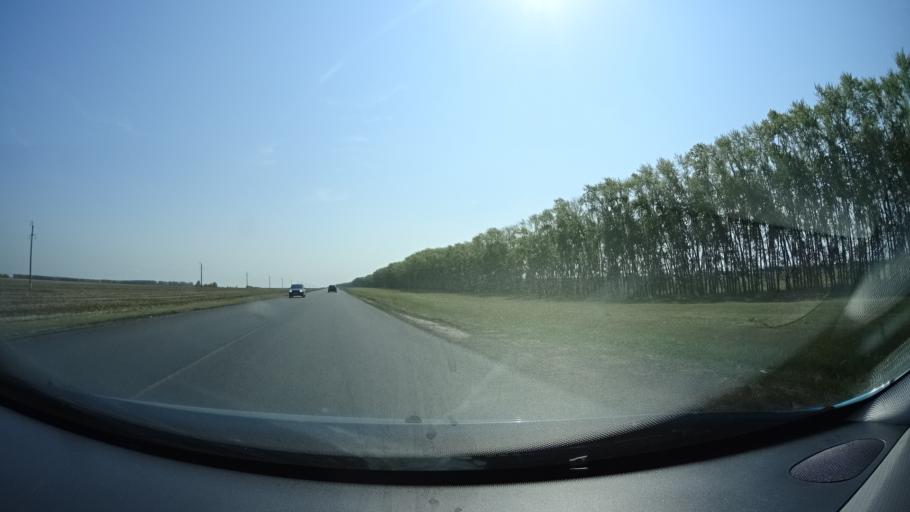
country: RU
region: Bashkortostan
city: Karmaskaly
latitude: 54.4136
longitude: 56.0602
